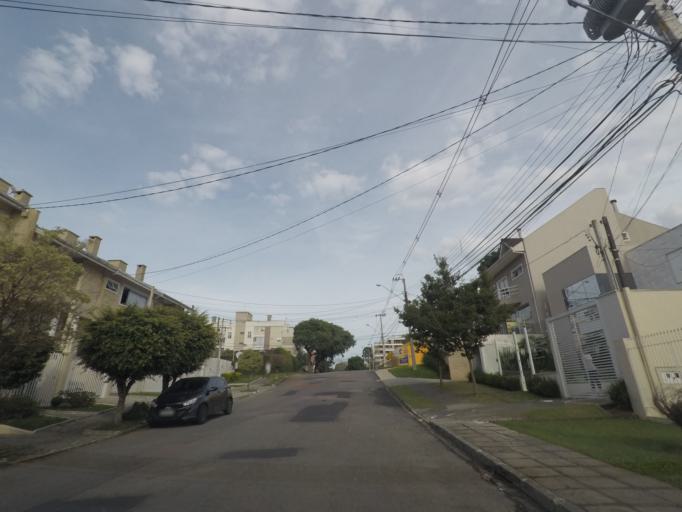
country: BR
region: Parana
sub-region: Curitiba
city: Curitiba
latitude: -25.4294
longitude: -49.2985
